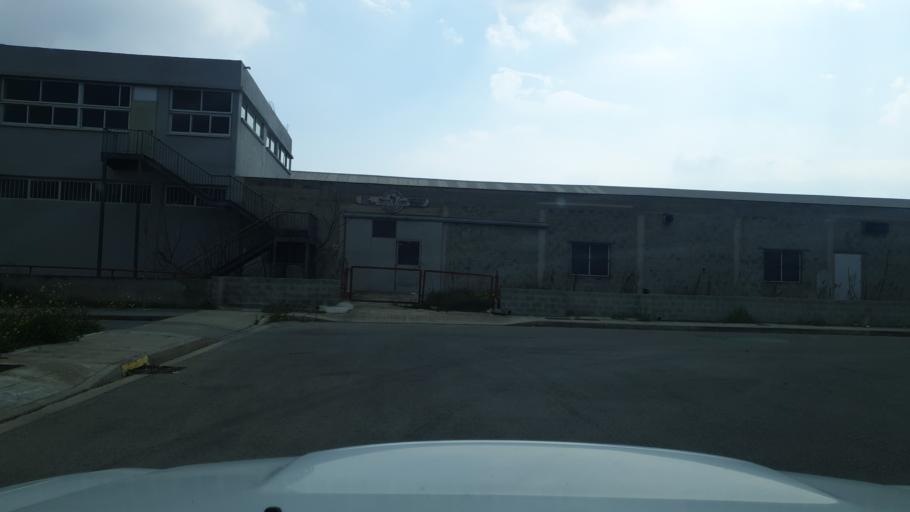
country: CY
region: Lefkosia
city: Geri
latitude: 35.0837
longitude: 33.3874
